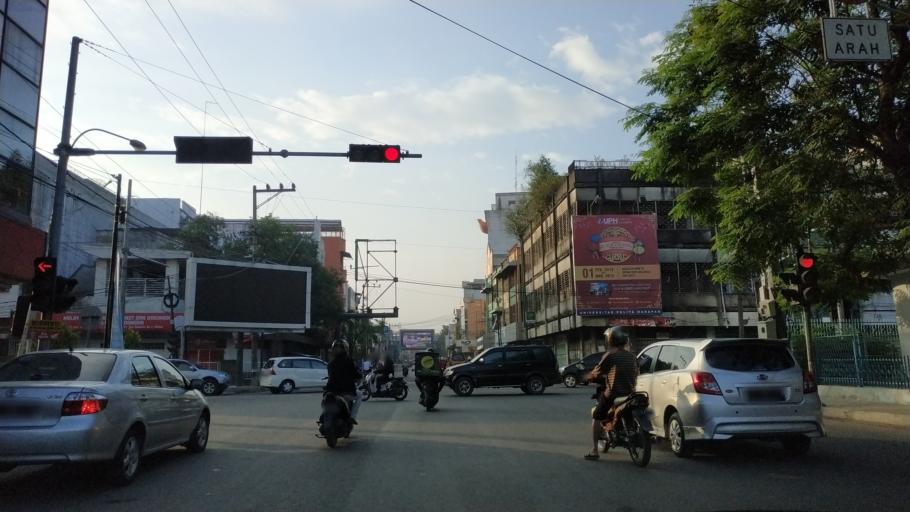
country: ID
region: North Sumatra
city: Medan
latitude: 3.5892
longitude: 98.6903
